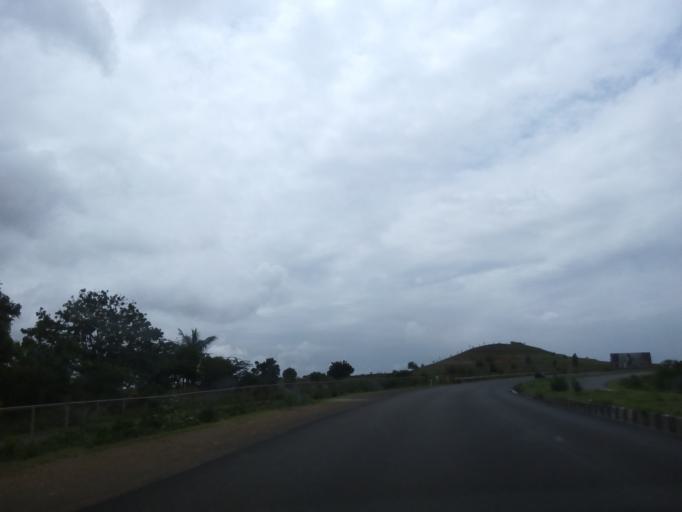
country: IN
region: Karnataka
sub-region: Haveri
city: Byadgi
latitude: 14.7156
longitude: 75.4993
